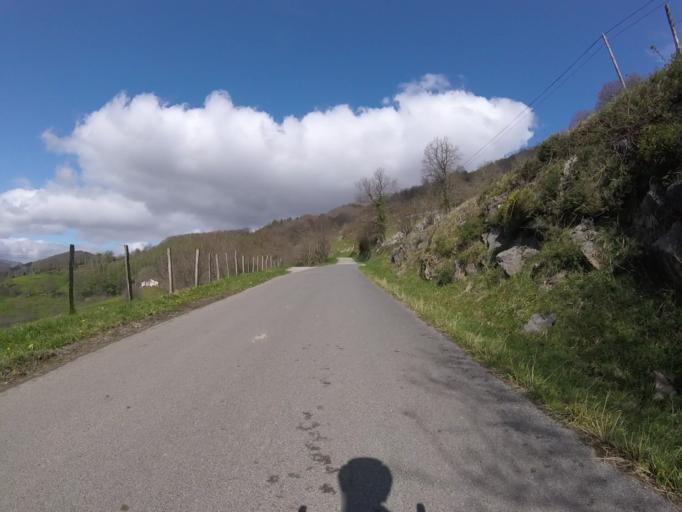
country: ES
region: Basque Country
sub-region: Provincia de Guipuzcoa
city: Albiztur
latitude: 43.1380
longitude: -2.1125
